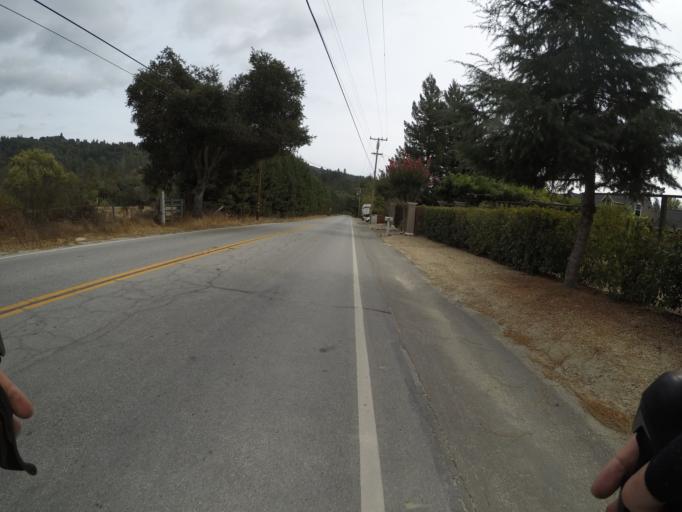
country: US
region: California
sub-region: Santa Cruz County
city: Mount Hermon
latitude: 37.0768
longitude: -122.0577
